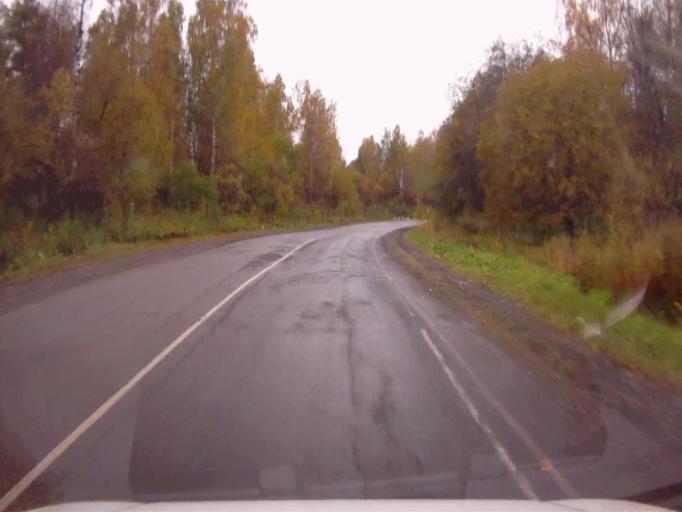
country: RU
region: Chelyabinsk
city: Nizhniy Ufaley
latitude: 56.0547
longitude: 60.0407
